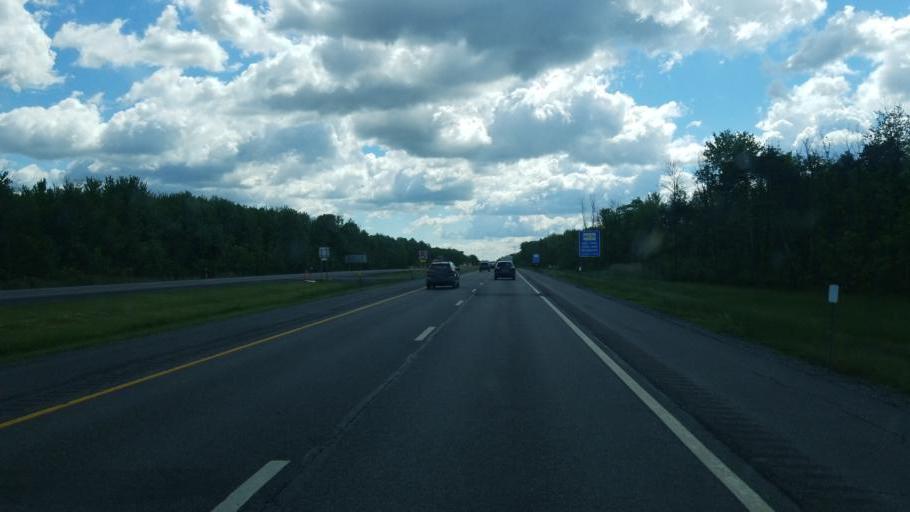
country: US
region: New York
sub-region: Onondaga County
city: Minoa
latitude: 43.0948
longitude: -76.0233
